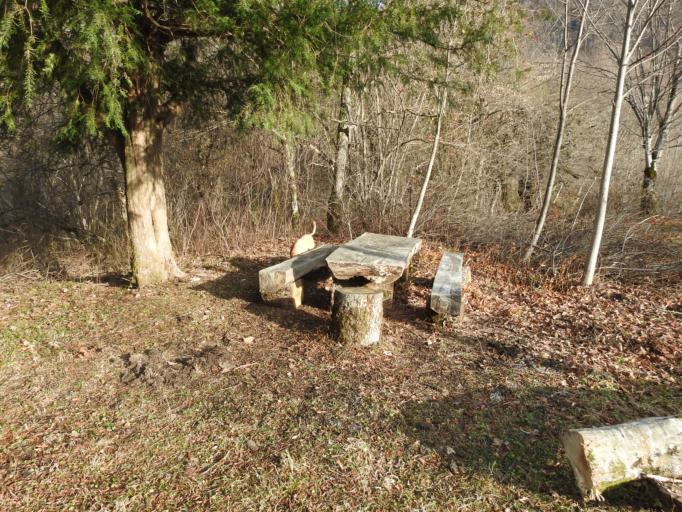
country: GE
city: Gantiadi
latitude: 43.4164
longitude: 40.2151
